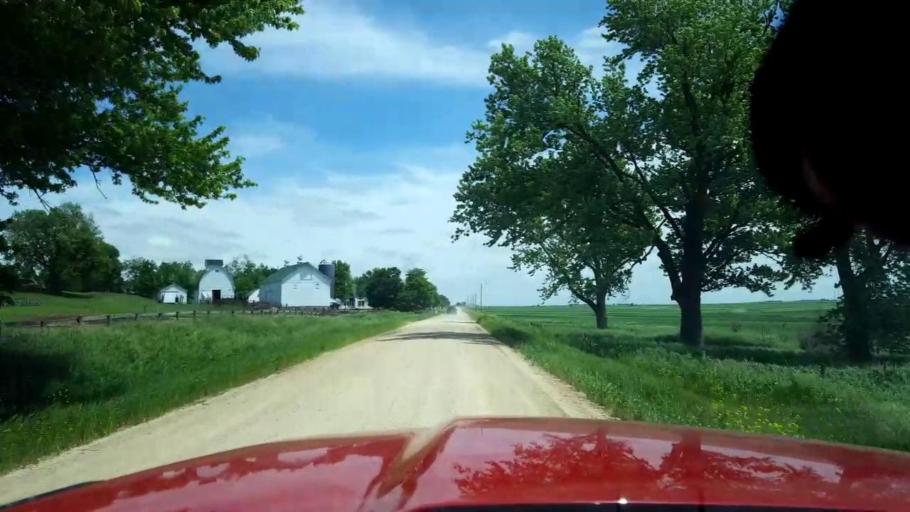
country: US
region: Iowa
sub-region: Linn County
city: Lisbon
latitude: 41.9546
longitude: -91.3613
